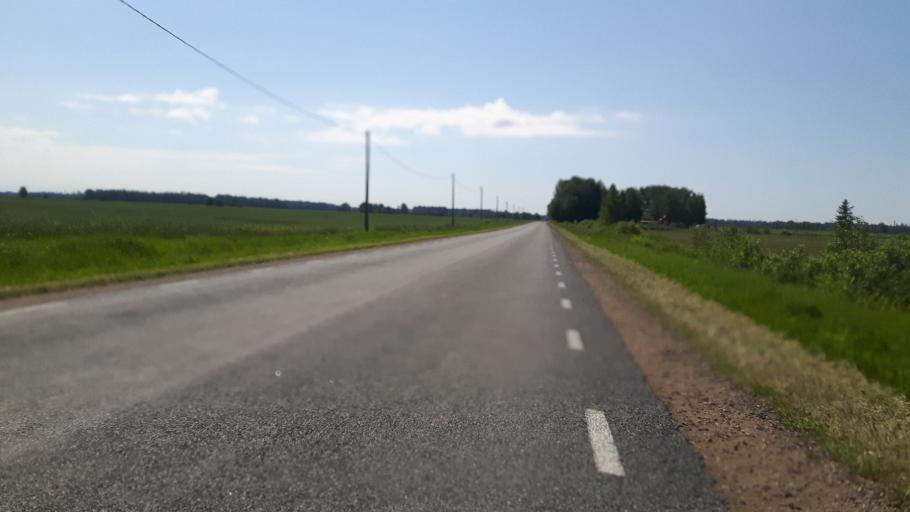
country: EE
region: Paernumaa
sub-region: Vaendra vald (alev)
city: Vandra
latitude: 58.6237
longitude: 25.0210
